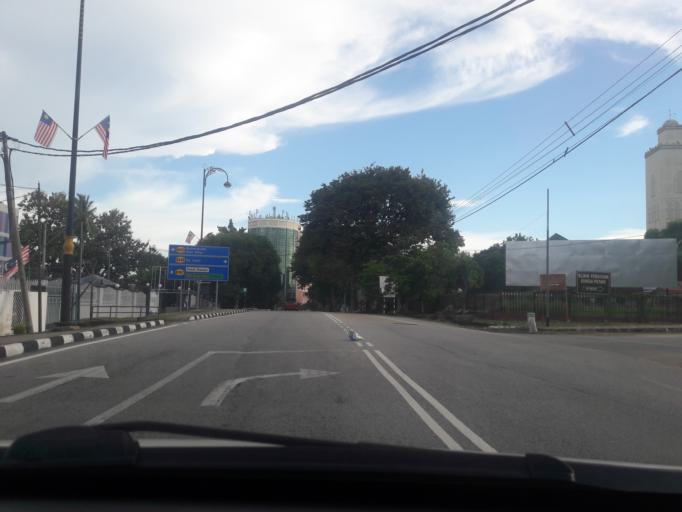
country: MY
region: Kedah
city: Sungai Petani
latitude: 5.6484
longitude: 100.4888
